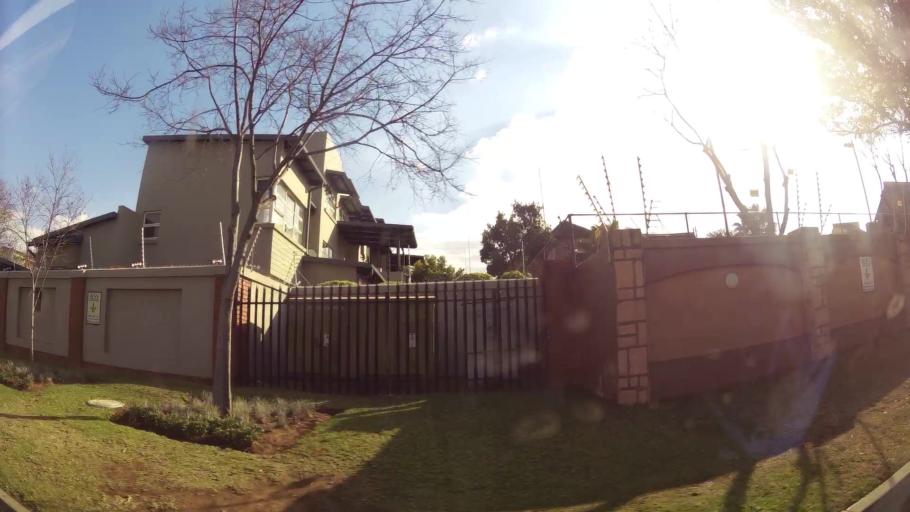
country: ZA
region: Gauteng
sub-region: City of Johannesburg Metropolitan Municipality
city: Diepsloot
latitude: -26.0193
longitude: 28.0165
